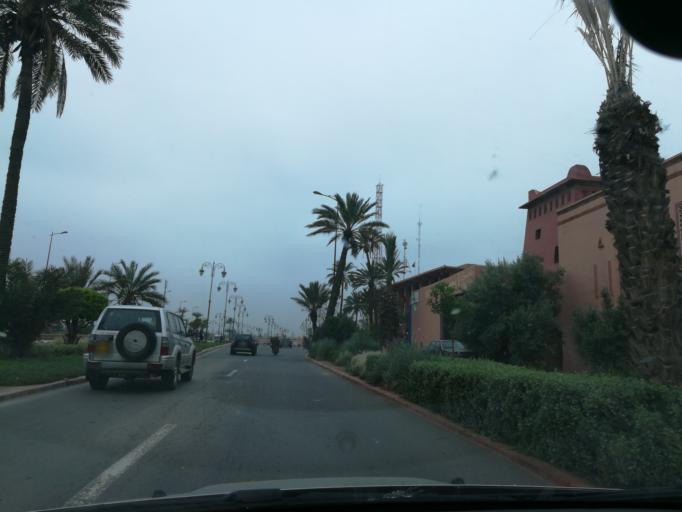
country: MA
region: Marrakech-Tensift-Al Haouz
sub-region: Marrakech
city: Marrakesh
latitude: 31.6480
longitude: -7.9867
